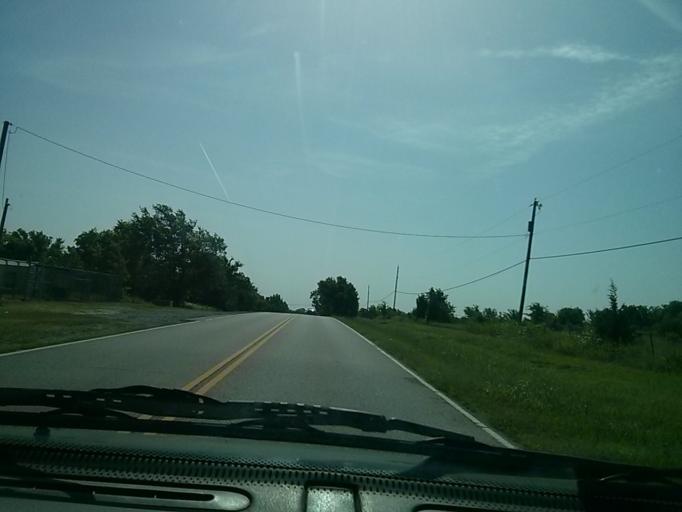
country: US
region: Oklahoma
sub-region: Rogers County
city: Catoosa
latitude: 36.1335
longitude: -95.7997
